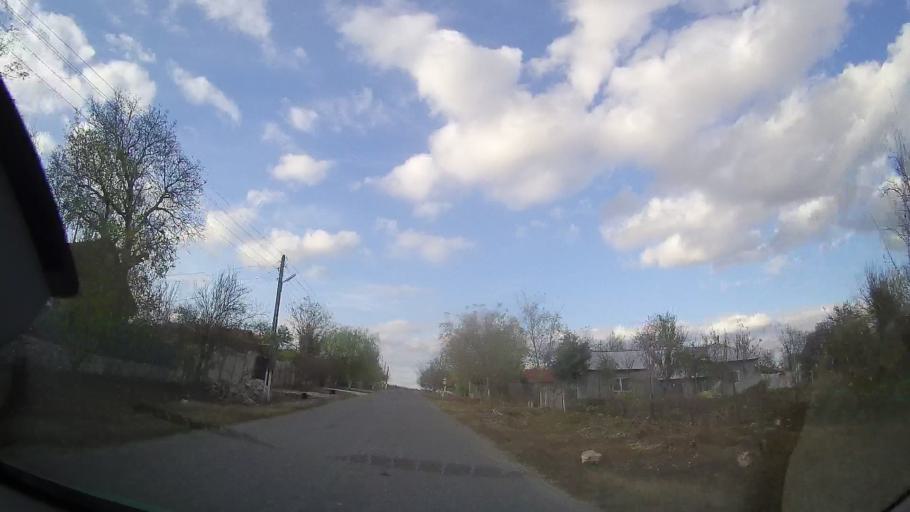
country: RO
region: Constanta
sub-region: Comuna Cerchezu
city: Cerchezu
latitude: 43.8628
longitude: 28.1005
